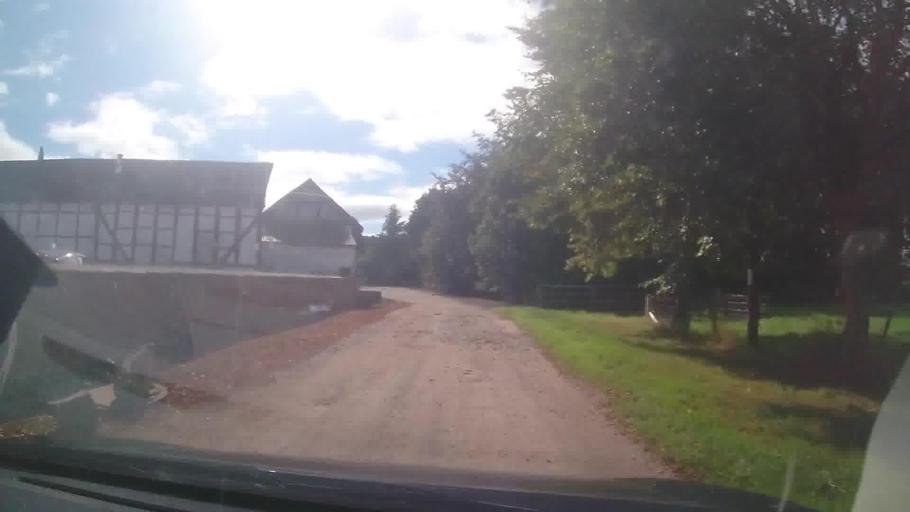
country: GB
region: England
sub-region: Shropshire
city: Prees
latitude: 52.8740
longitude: -2.6320
